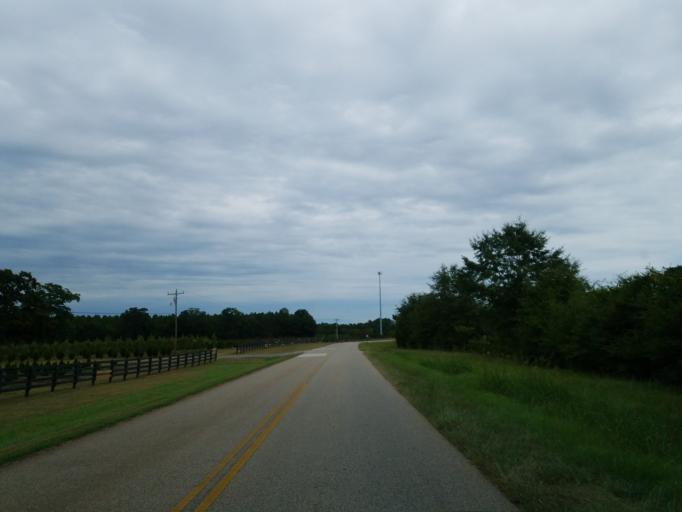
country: US
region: Georgia
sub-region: Monroe County
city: Forsyth
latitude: 32.9813
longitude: -84.0097
